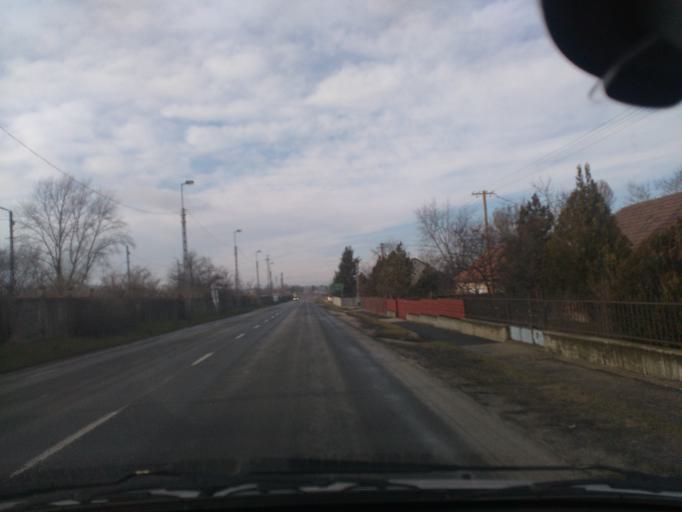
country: HU
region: Komarom-Esztergom
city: Tokod
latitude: 47.7335
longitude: 18.6844
